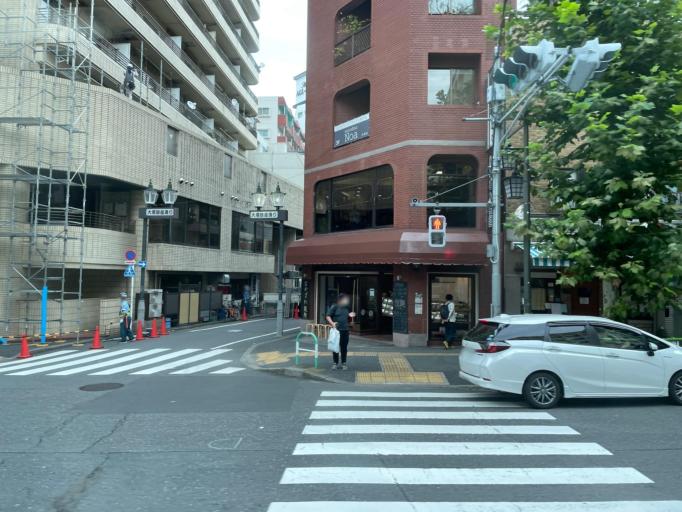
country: JP
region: Tokyo
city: Tokyo
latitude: 35.7299
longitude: 139.7293
